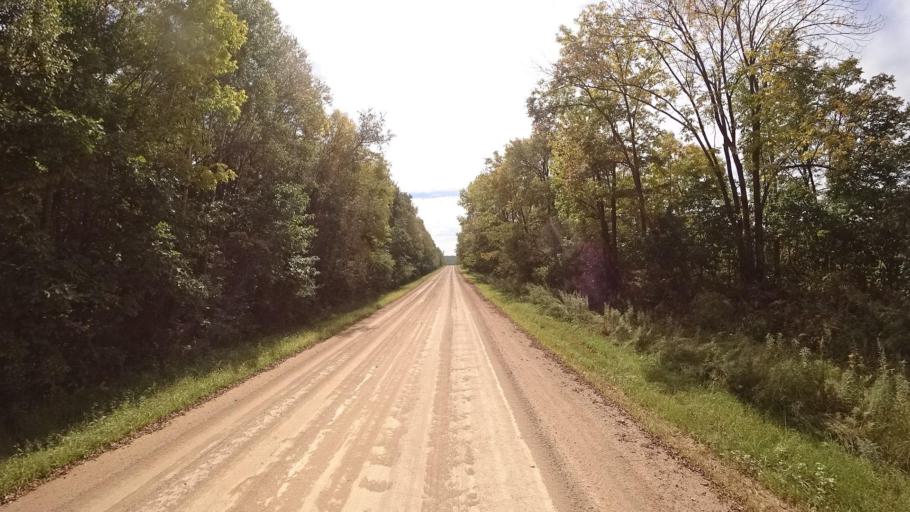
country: RU
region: Primorskiy
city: Yakovlevka
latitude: 44.6289
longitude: 133.6013
